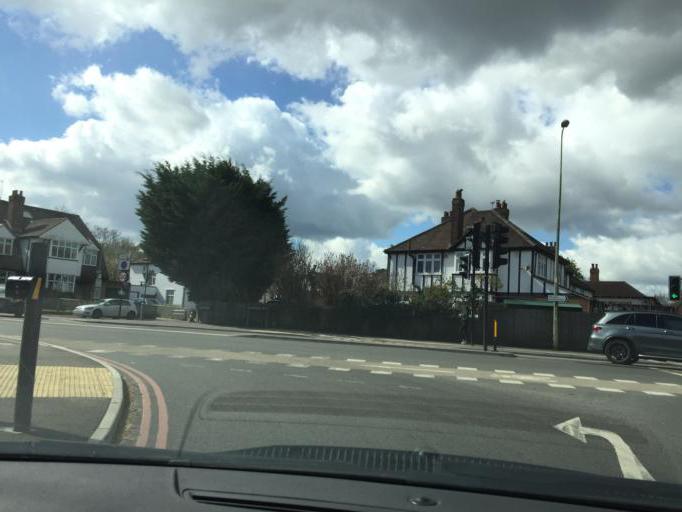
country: GB
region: England
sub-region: Oxfordshire
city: Oxford
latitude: 51.7636
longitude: -1.2252
